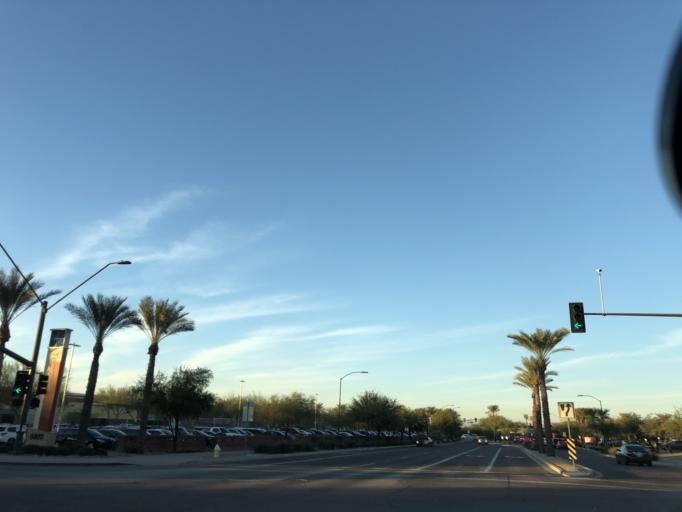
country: US
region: Arizona
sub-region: Maricopa County
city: Peoria
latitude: 33.5330
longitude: -112.2648
